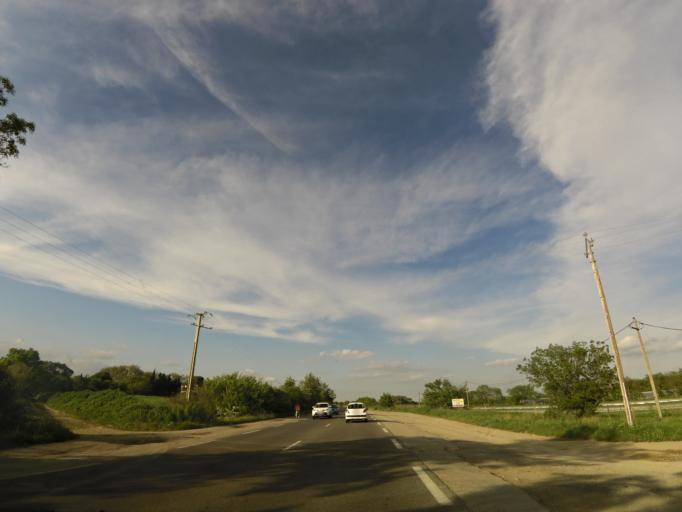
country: FR
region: Languedoc-Roussillon
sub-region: Departement de l'Herault
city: Saint-Just
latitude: 43.6391
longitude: 4.1364
